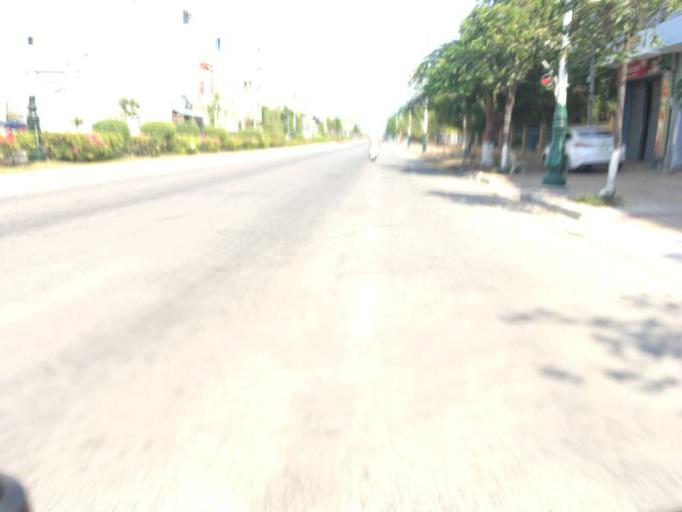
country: VN
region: Ninh Thuan
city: Phan Rang-Thap Cham
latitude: 11.5634
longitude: 109.0159
